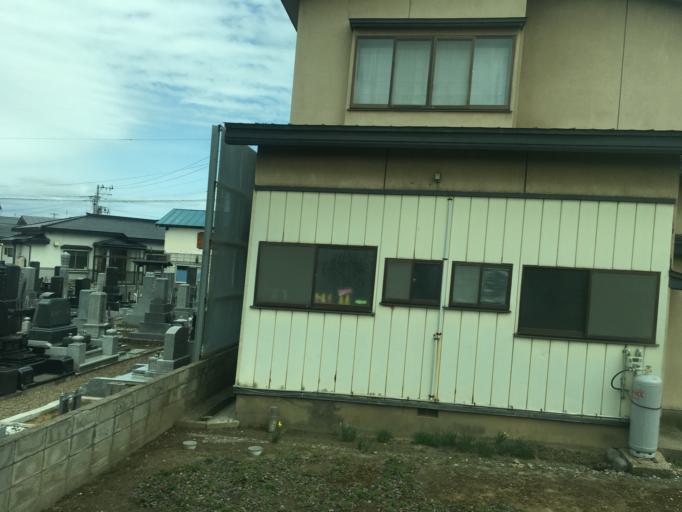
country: JP
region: Aomori
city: Hirosaki
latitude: 40.6557
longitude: 140.4982
